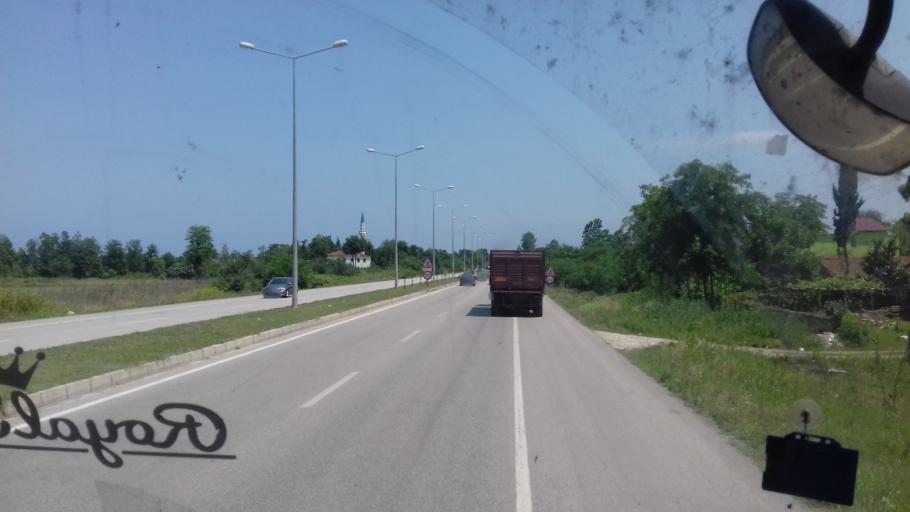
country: TR
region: Samsun
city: Terme
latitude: 41.1677
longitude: 37.0614
